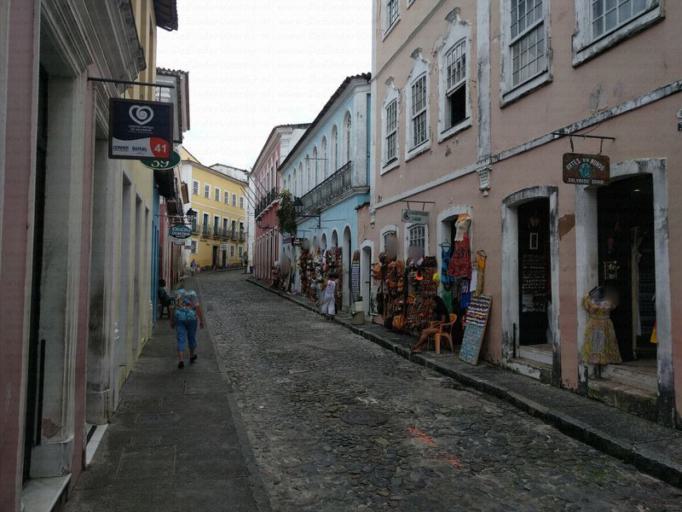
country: BR
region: Bahia
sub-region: Salvador
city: Salvador
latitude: -12.9718
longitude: -38.5084
